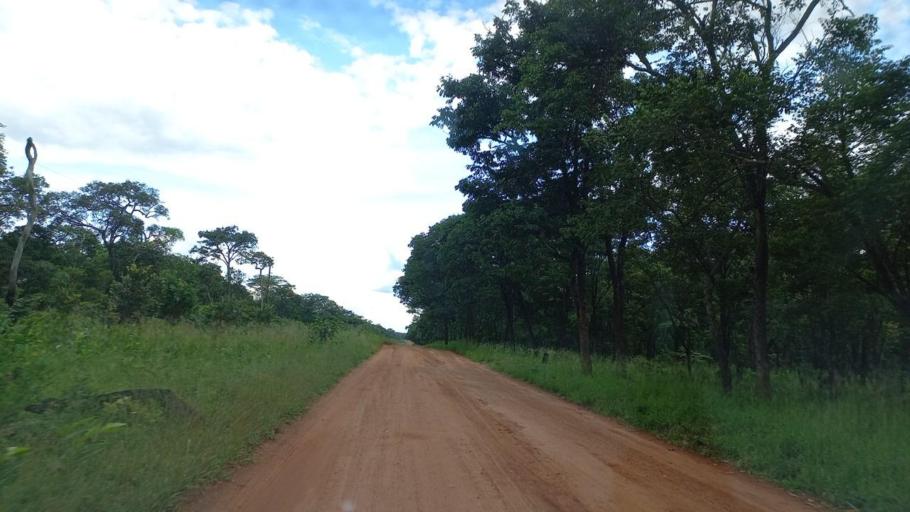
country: ZM
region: North-Western
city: Mwinilunga
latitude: -11.8056
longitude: 24.3691
